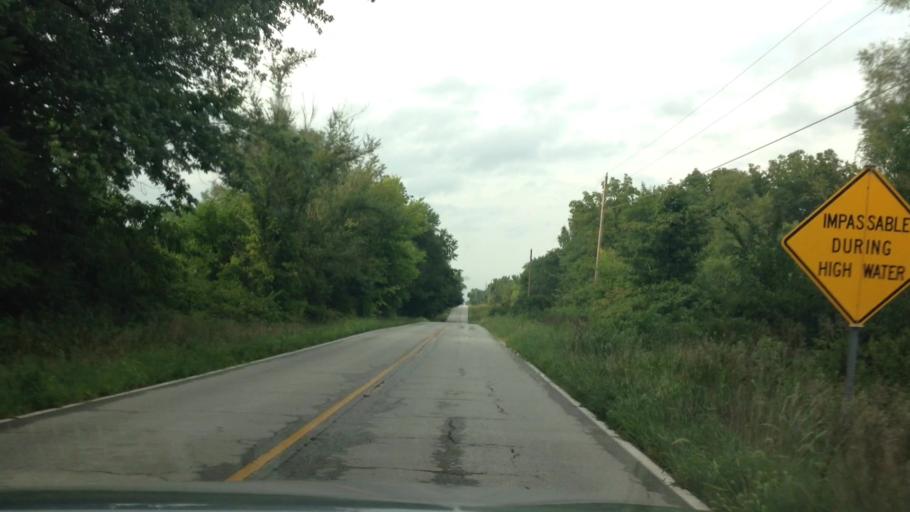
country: US
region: Missouri
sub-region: Clay County
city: Smithville
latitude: 39.3699
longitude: -94.6671
